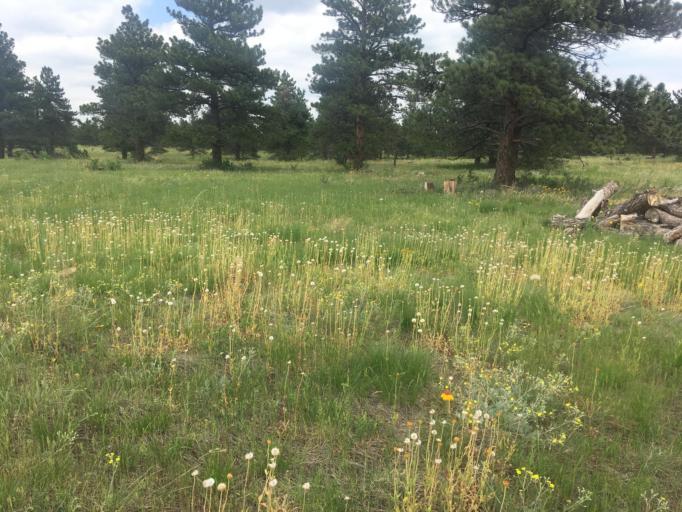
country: US
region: Colorado
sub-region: Boulder County
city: Superior
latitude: 39.9166
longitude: -105.2521
